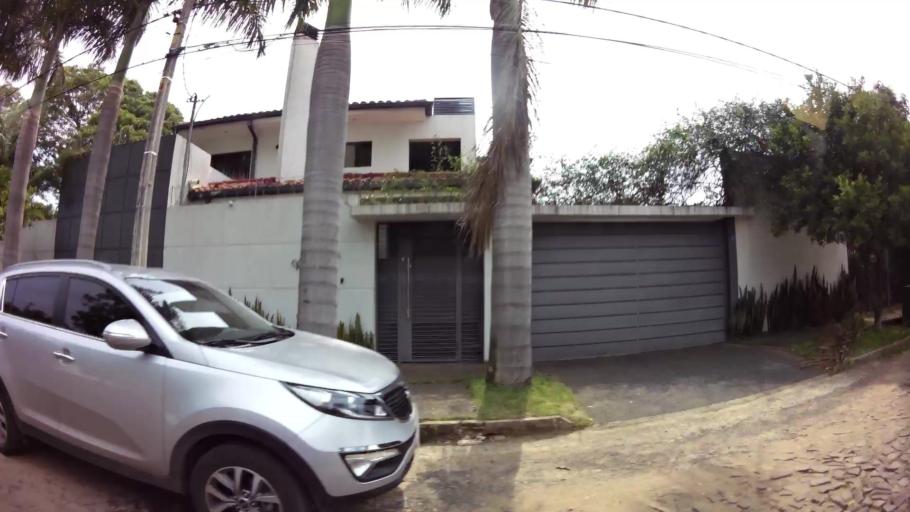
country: PY
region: Asuncion
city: Asuncion
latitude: -25.2799
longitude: -57.5689
